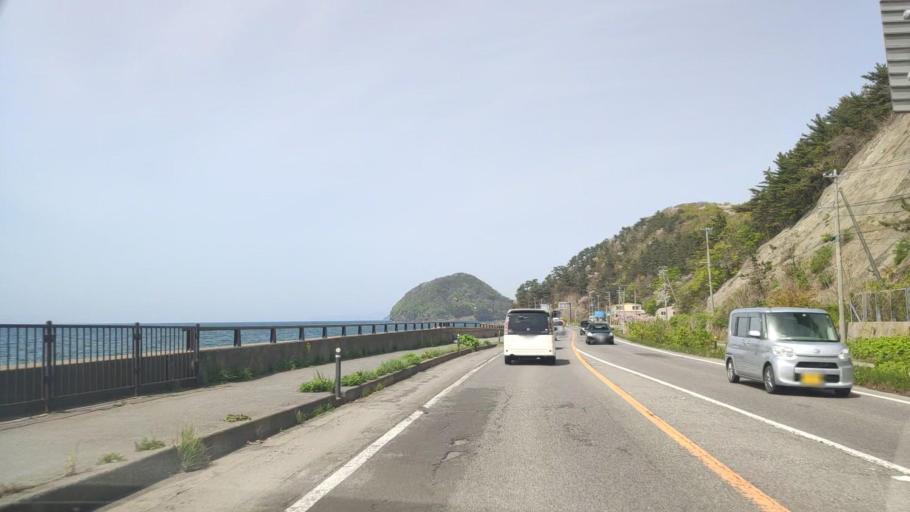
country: JP
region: Aomori
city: Aomori Shi
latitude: 40.8787
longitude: 140.8498
